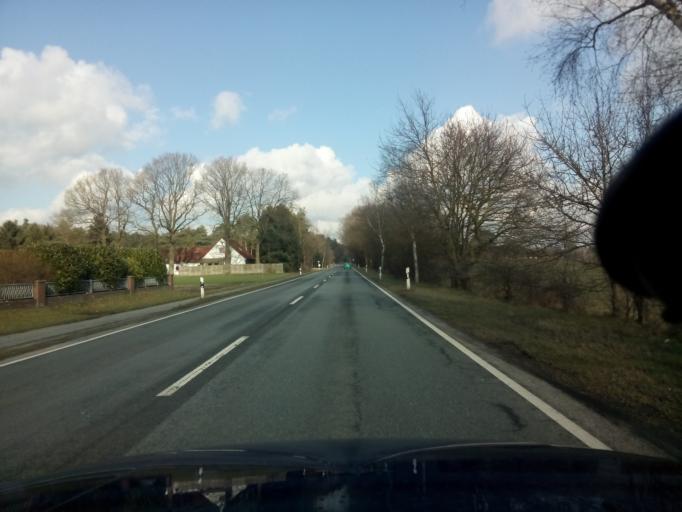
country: DE
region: Lower Saxony
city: Hambergen
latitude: 53.2757
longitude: 8.8205
